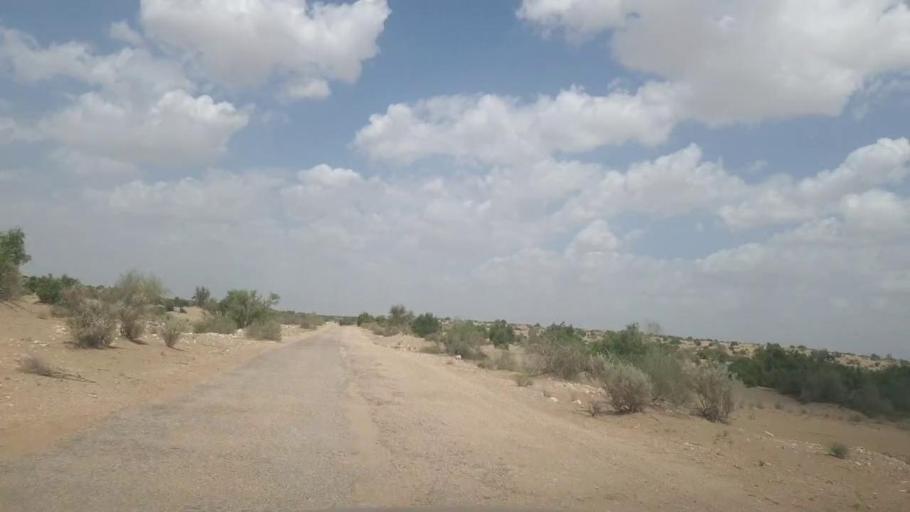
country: PK
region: Sindh
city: Kot Diji
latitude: 27.2693
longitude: 69.1896
